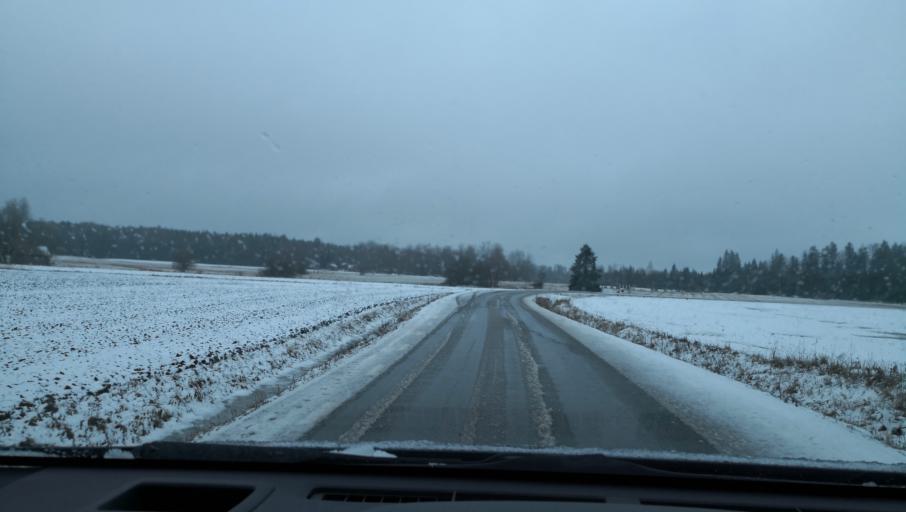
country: SE
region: Vaestmanland
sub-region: Hallstahammars Kommun
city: Hallstahammar
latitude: 59.5974
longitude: 16.1420
